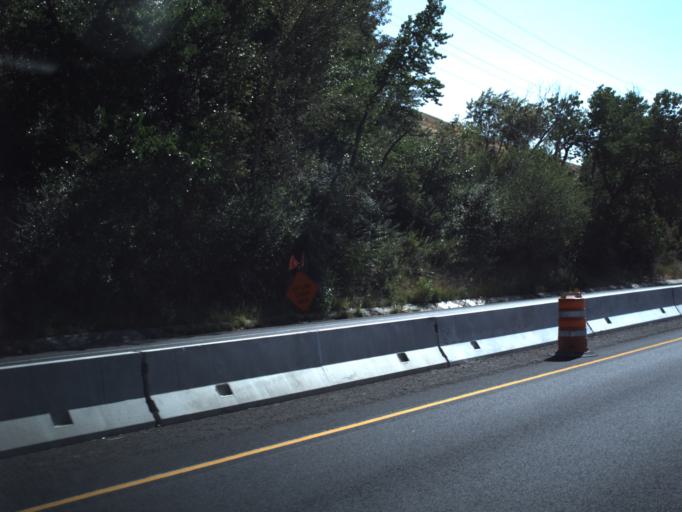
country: US
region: Utah
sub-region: Box Elder County
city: Brigham City
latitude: 41.4894
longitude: -112.0022
